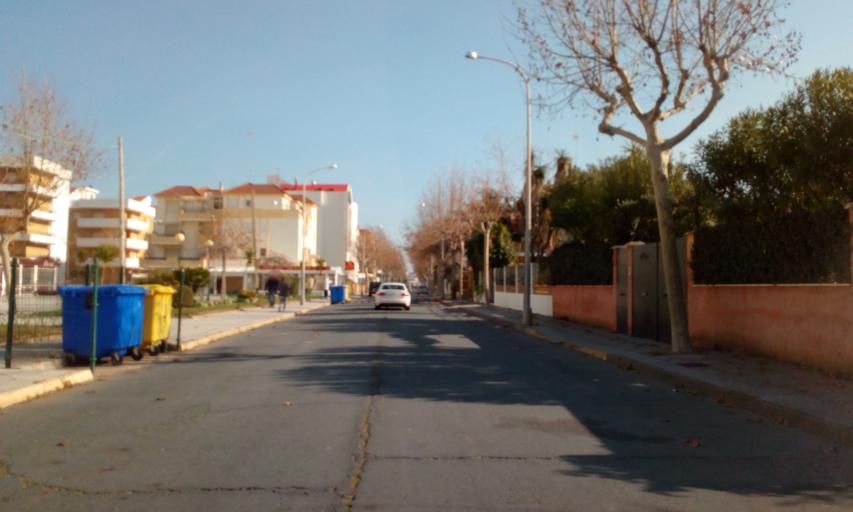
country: ES
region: Andalusia
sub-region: Provincia de Huelva
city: Lepe
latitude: 37.2067
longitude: -7.2125
